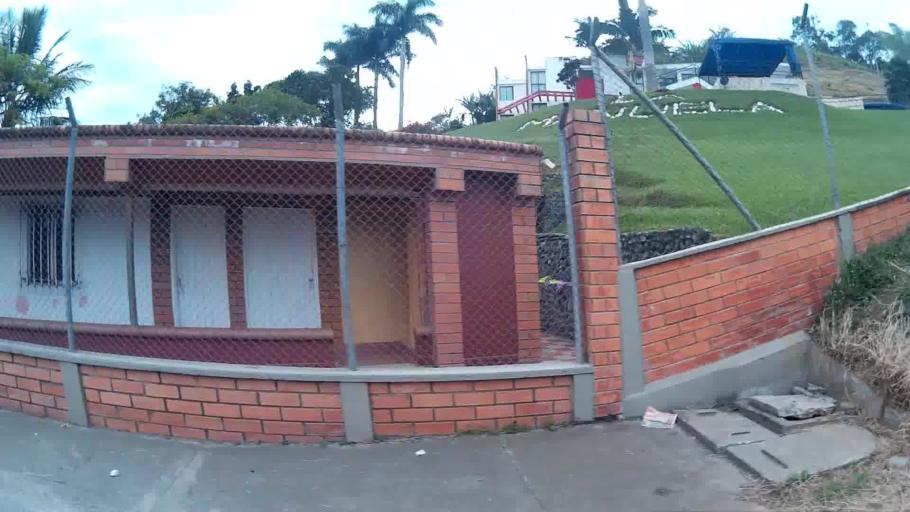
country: CO
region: Risaralda
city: Pereira
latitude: 4.7655
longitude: -75.7194
